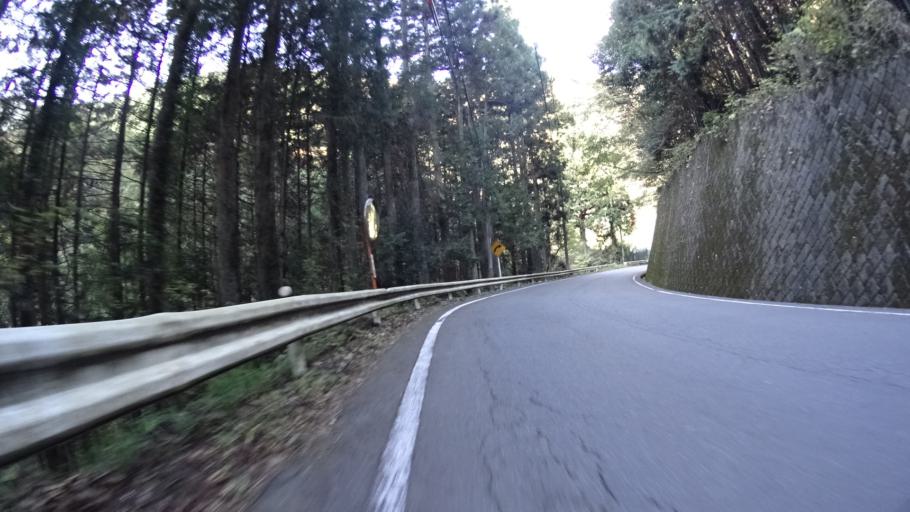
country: JP
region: Yamanashi
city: Uenohara
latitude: 35.6802
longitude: 139.0578
